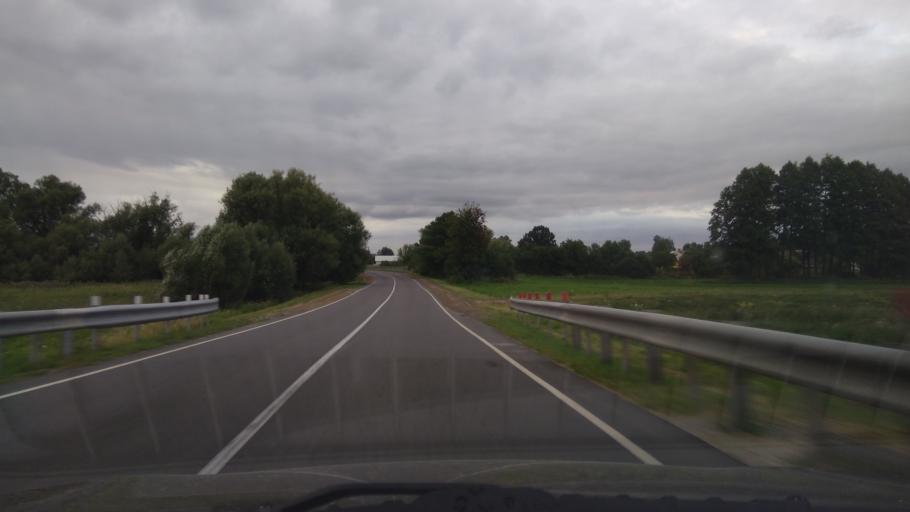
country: BY
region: Brest
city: Byaroza
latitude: 52.4190
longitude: 24.9802
